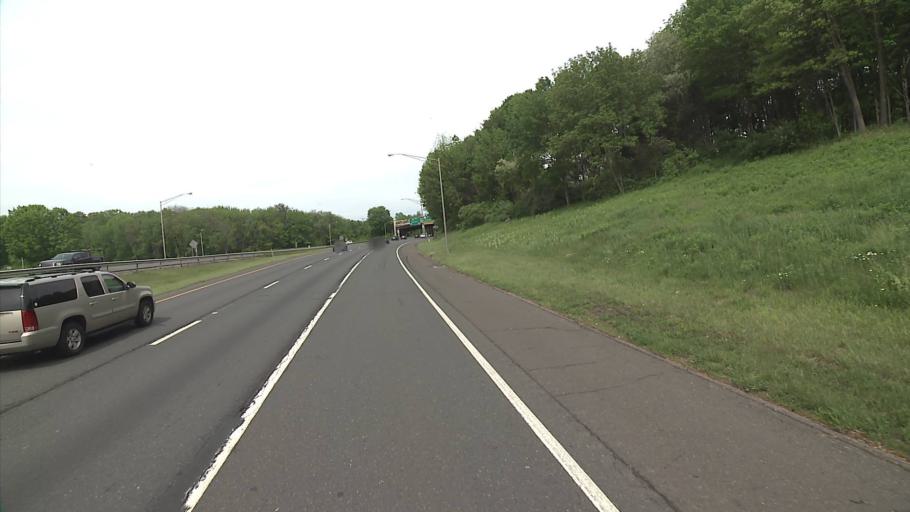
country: US
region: Connecticut
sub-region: Fairfield County
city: Newtown
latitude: 41.4170
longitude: -73.2877
